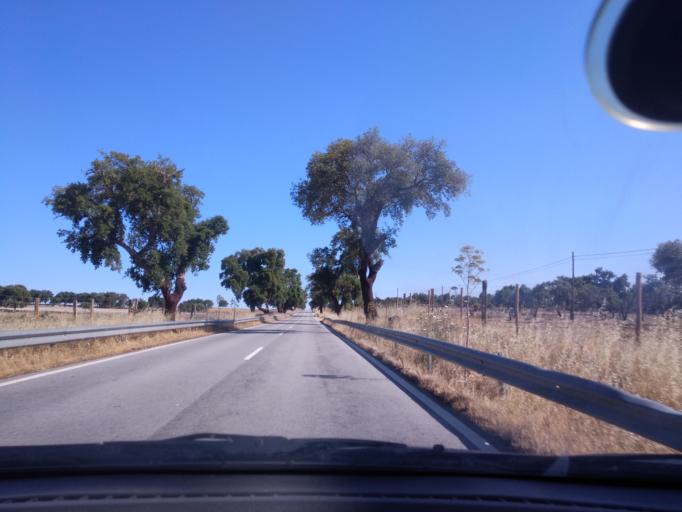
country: PT
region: Portalegre
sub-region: Nisa
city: Nisa
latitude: 39.4512
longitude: -7.6288
